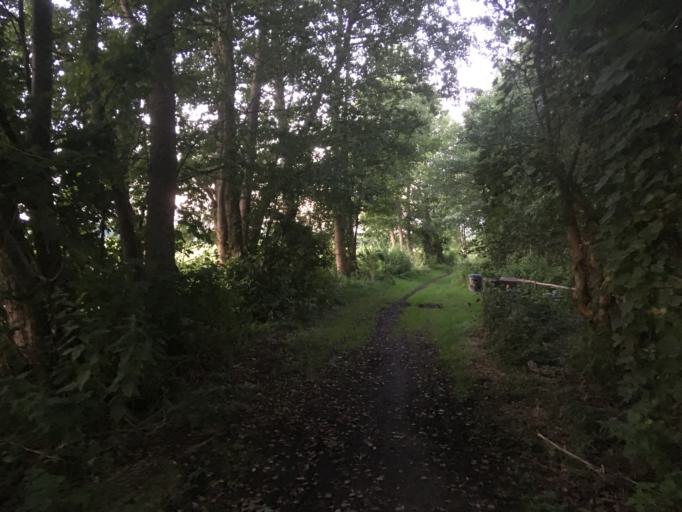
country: DE
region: Brandenburg
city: Erkner
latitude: 52.4135
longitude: 13.7436
